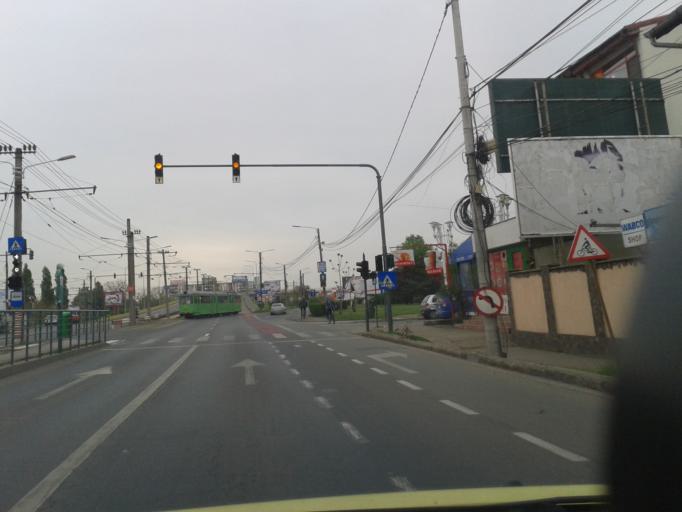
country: RO
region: Arad
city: Arad
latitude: 46.1810
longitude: 21.3328
